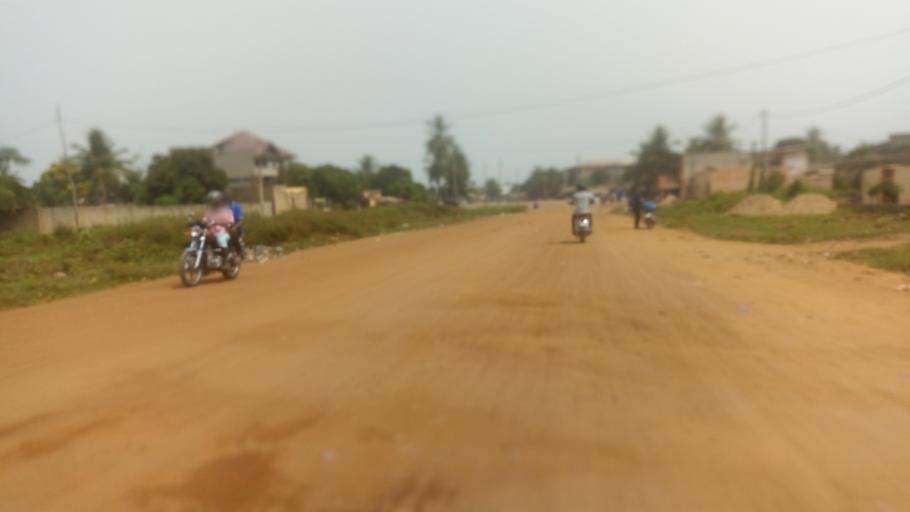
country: TG
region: Maritime
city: Lome
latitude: 6.1849
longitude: 1.1722
